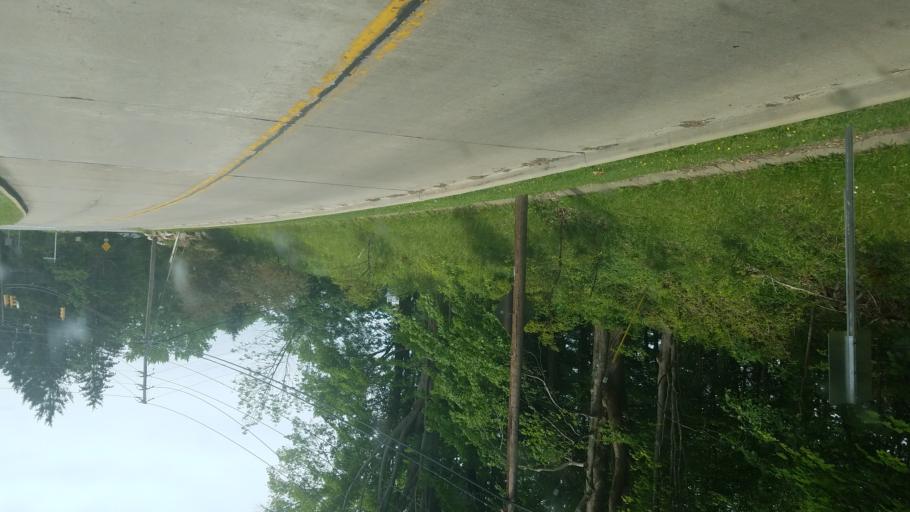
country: US
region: Ohio
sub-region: Cuyahoga County
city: Chagrin Falls
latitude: 41.4126
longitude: -81.4117
